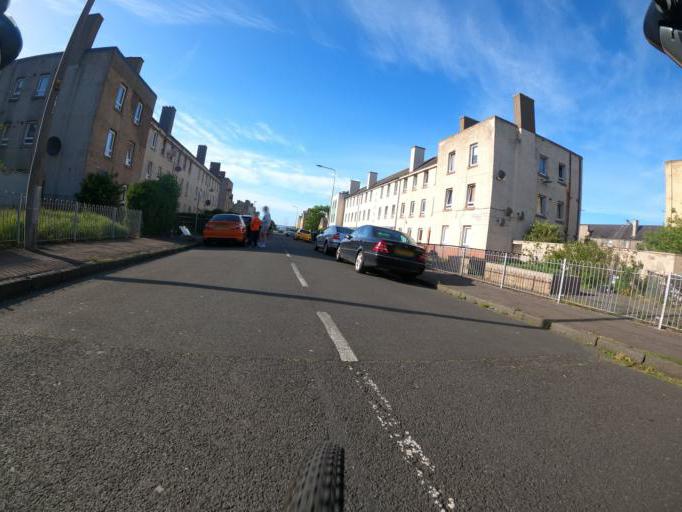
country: GB
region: Scotland
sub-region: Edinburgh
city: Edinburgh
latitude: 55.9771
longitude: -3.2253
